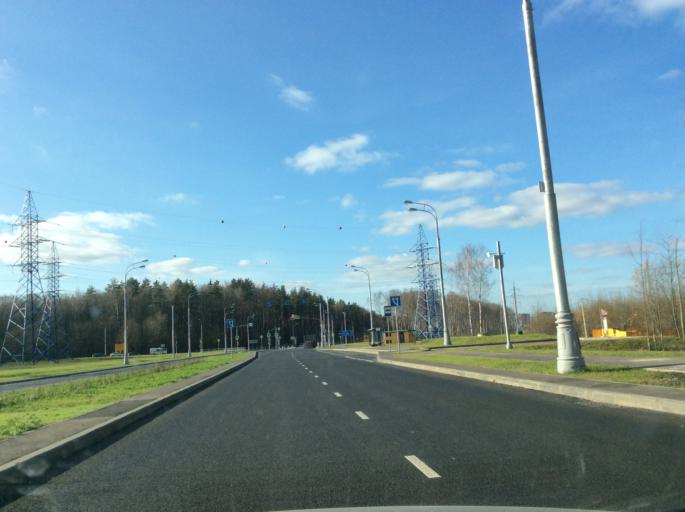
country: RU
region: Moskovskaya
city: Vatutinki
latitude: 55.4840
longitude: 37.3388
